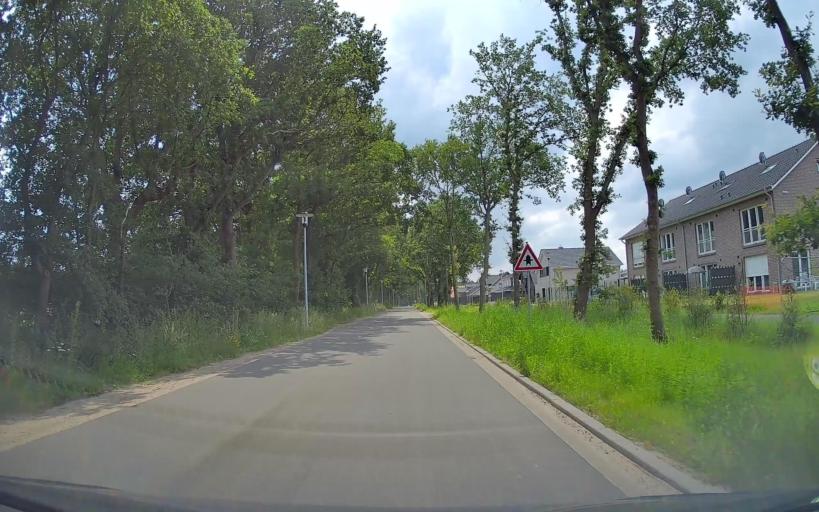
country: DE
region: Lower Saxony
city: Bosel
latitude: 53.0013
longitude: 7.9636
